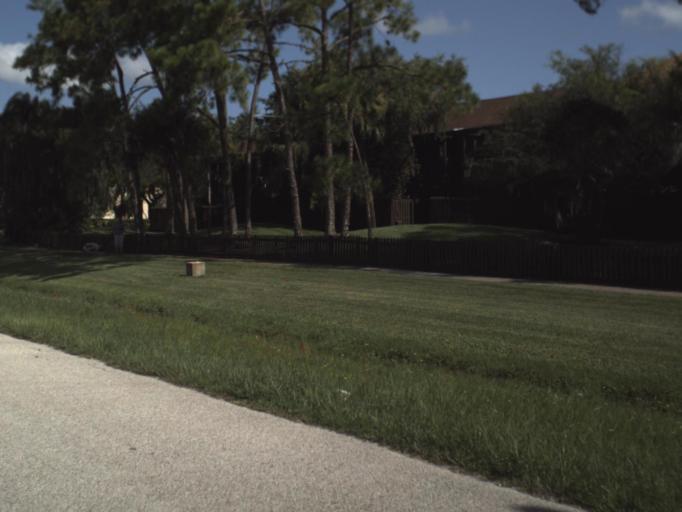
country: US
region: Florida
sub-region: Pinellas County
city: Gandy
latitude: 27.8684
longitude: -82.6448
